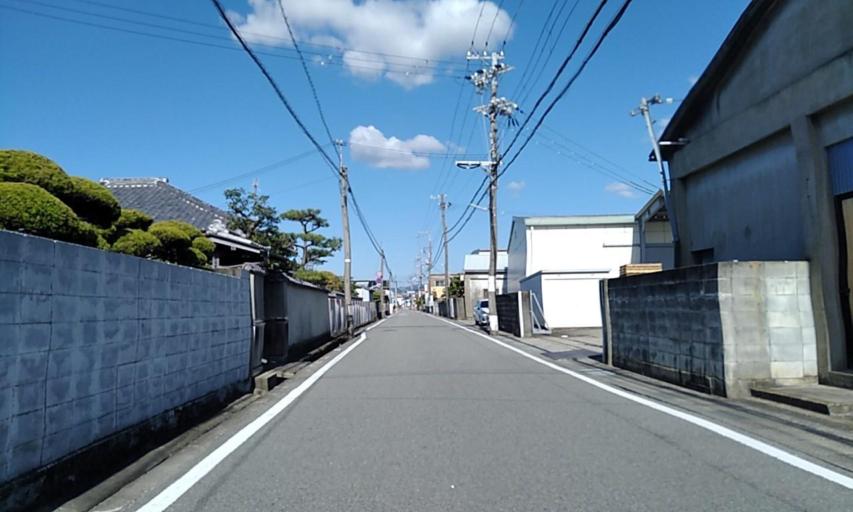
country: JP
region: Wakayama
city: Kainan
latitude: 34.1863
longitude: 135.1882
